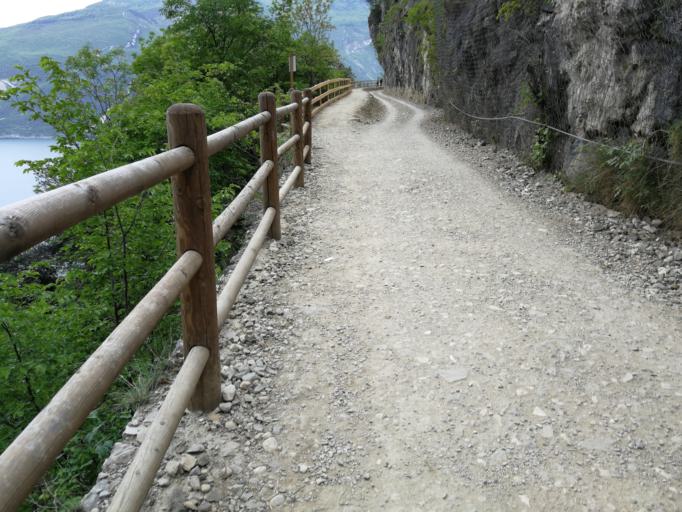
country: IT
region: Trentino-Alto Adige
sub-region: Provincia di Trento
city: Riva del Garda
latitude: 45.8696
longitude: 10.8335
